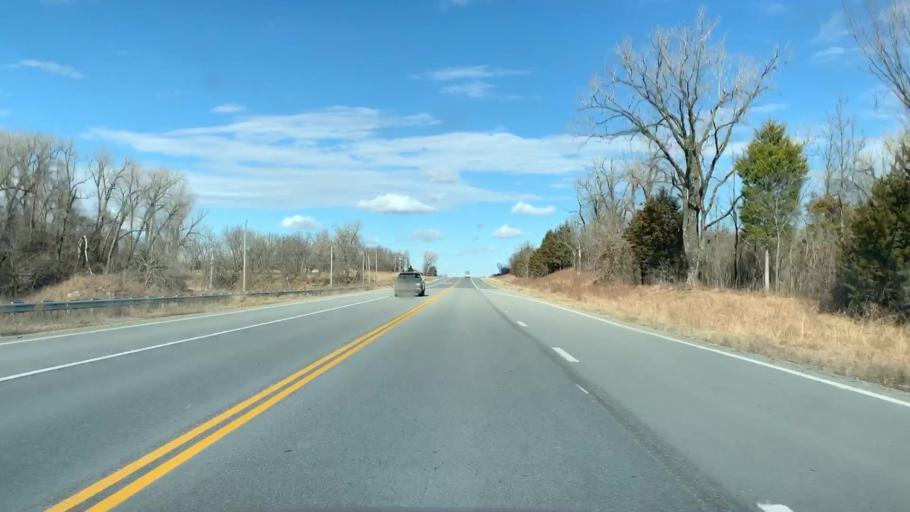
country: US
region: Kansas
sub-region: Cherokee County
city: Columbus
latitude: 37.3215
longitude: -94.8323
